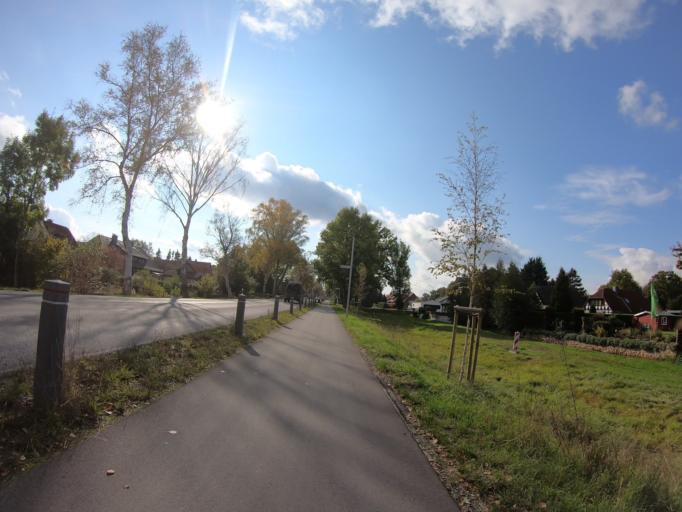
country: DE
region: Lower Saxony
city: Sassenburg
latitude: 52.5305
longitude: 10.5982
